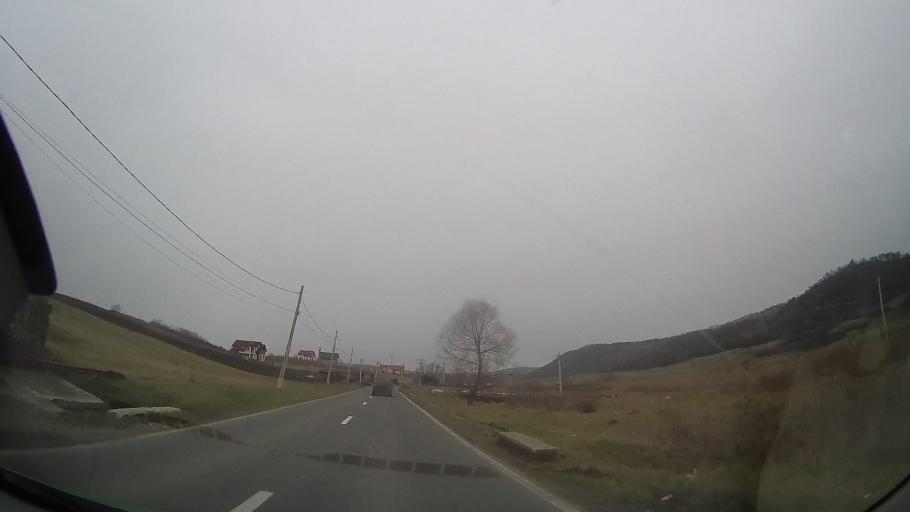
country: RO
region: Mures
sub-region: Comuna Ceausu de Campie
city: Ceausu de Campie
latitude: 46.6232
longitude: 24.5226
